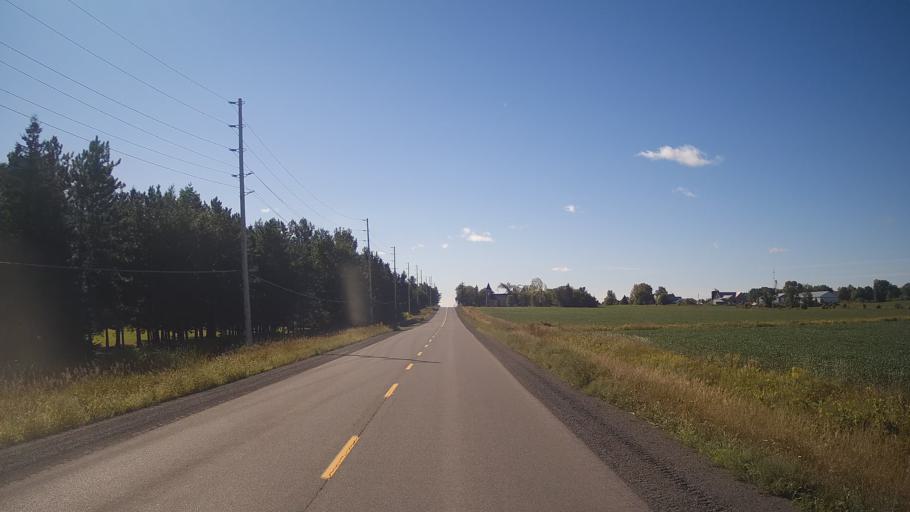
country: CA
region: Ontario
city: Prescott
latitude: 44.9740
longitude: -75.5354
